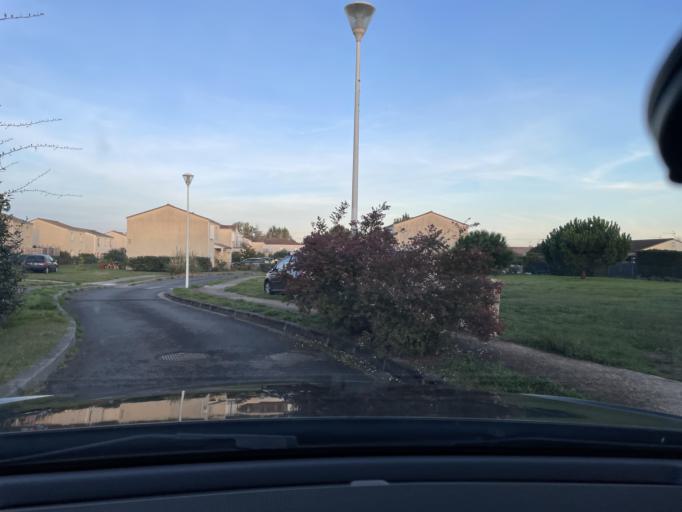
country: FR
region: Aquitaine
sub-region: Departement de la Gironde
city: Villenave-d'Ornon
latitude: 44.7795
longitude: -0.5425
